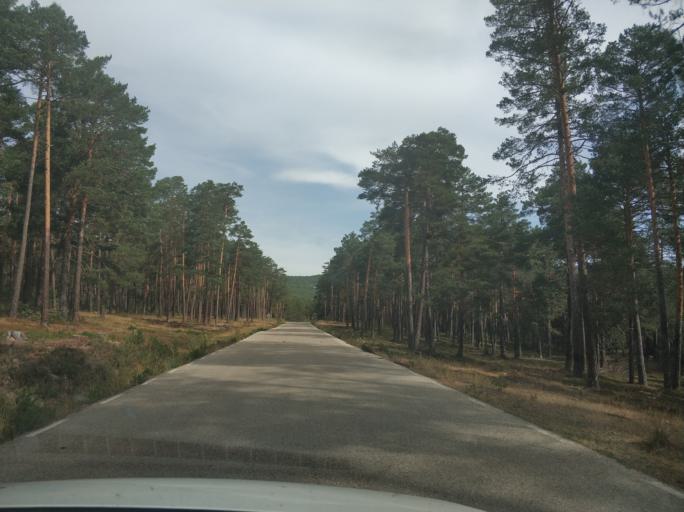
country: ES
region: Castille and Leon
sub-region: Provincia de Soria
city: Navaleno
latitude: 41.8729
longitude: -2.9387
